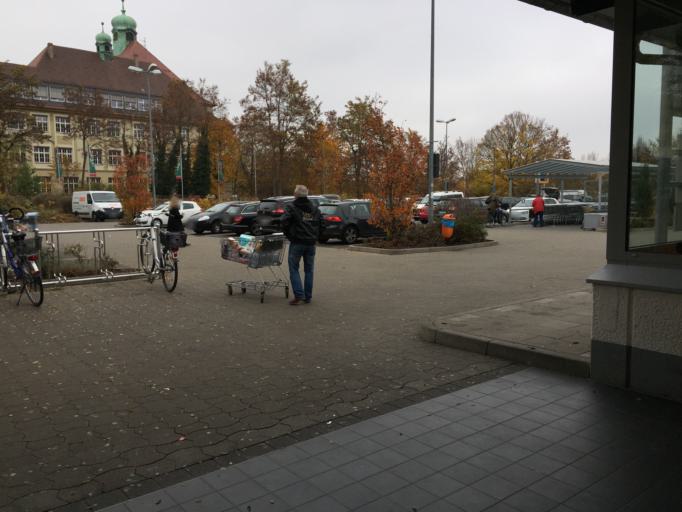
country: DE
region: Bavaria
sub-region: Regierungsbezirk Mittelfranken
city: Wetzendorf
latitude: 49.4547
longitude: 11.0522
